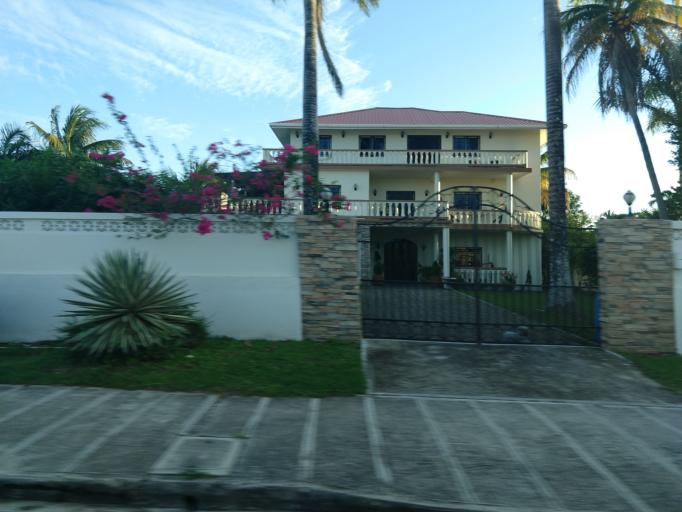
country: BZ
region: Belize
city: Belize City
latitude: 17.5123
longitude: -88.1906
